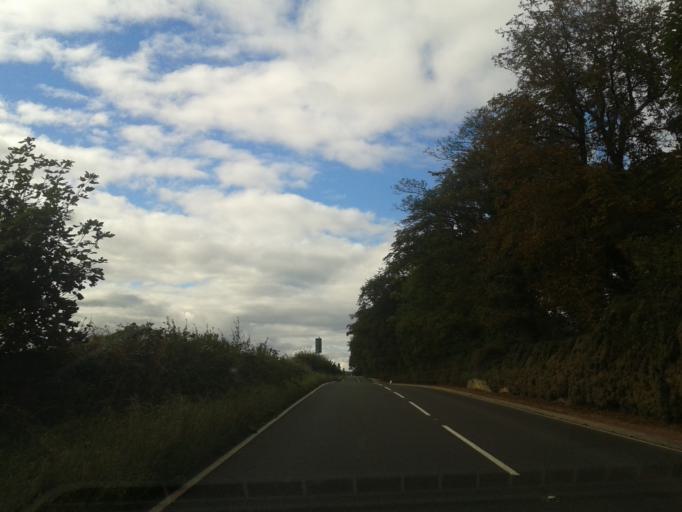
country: GB
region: Scotland
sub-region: Fife
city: Leuchars
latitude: 56.3593
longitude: -2.8943
